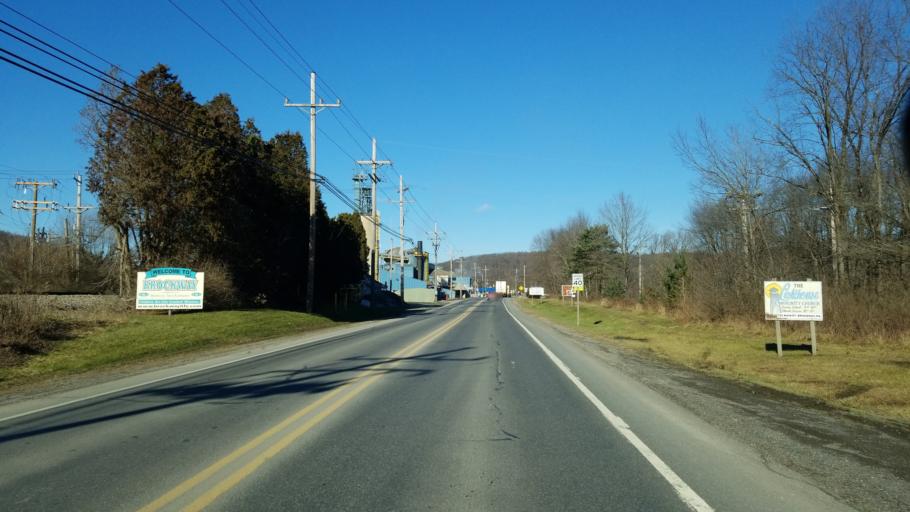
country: US
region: Pennsylvania
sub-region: Jefferson County
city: Brockway
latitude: 41.2394
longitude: -78.7841
